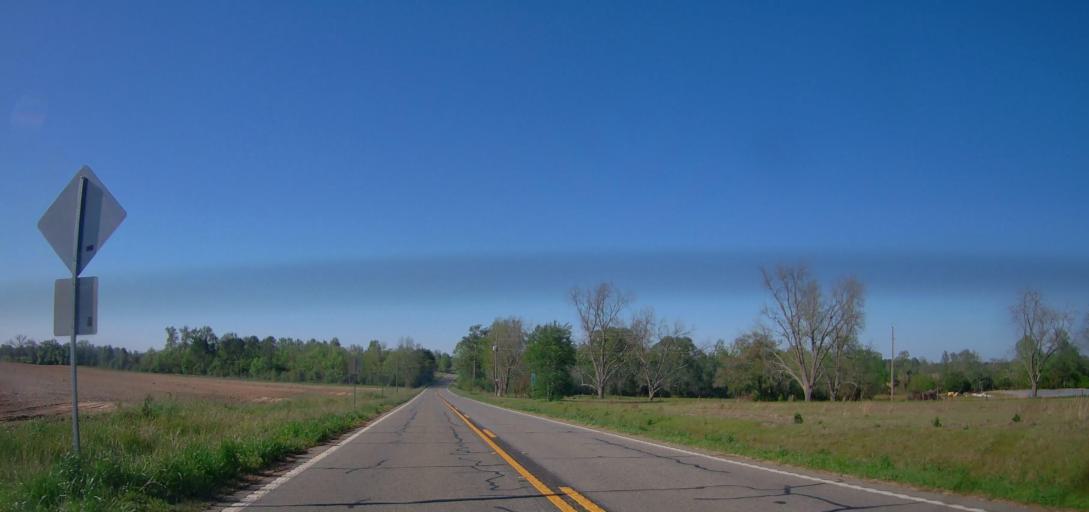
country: US
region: Georgia
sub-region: Wilcox County
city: Rochelle
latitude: 31.8119
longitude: -83.4890
